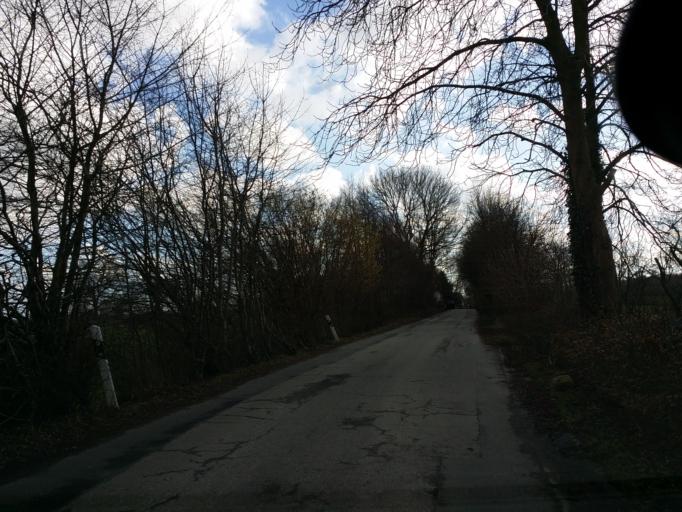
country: DE
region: Schleswig-Holstein
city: Krummwisch
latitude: 54.3097
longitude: 9.9055
